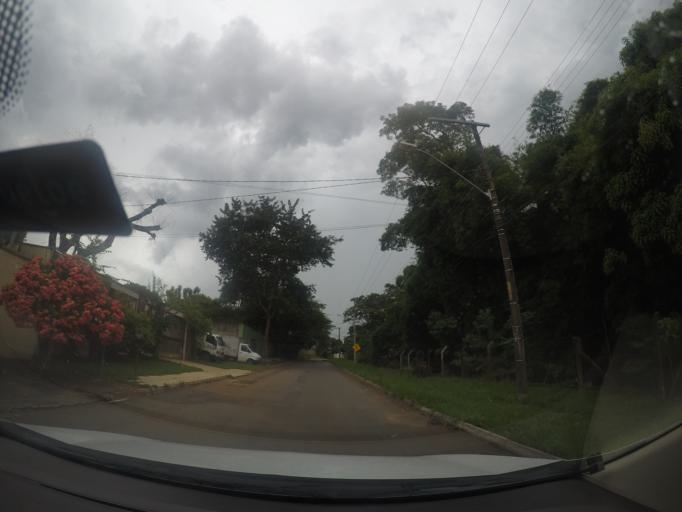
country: BR
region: Goias
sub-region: Goiania
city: Goiania
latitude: -16.6431
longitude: -49.2237
